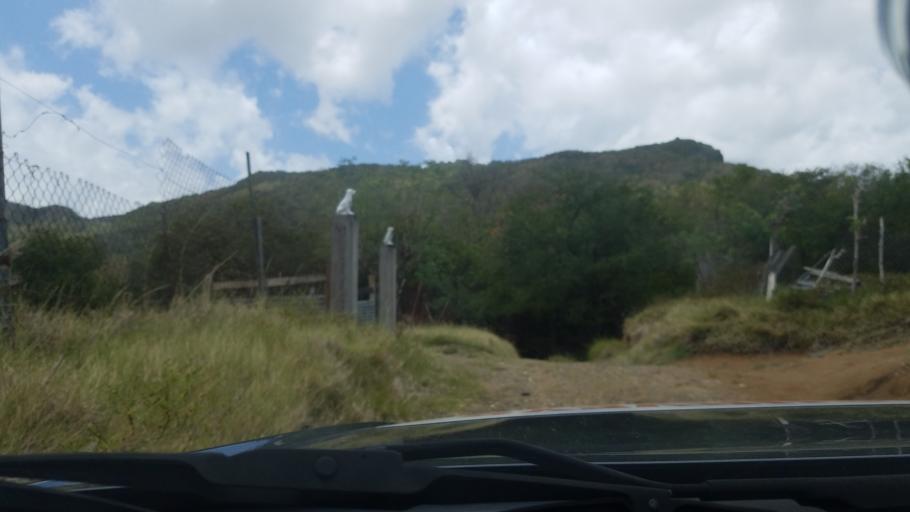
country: LC
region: Gros-Islet
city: Gros Islet
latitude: 14.0539
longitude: -60.9338
